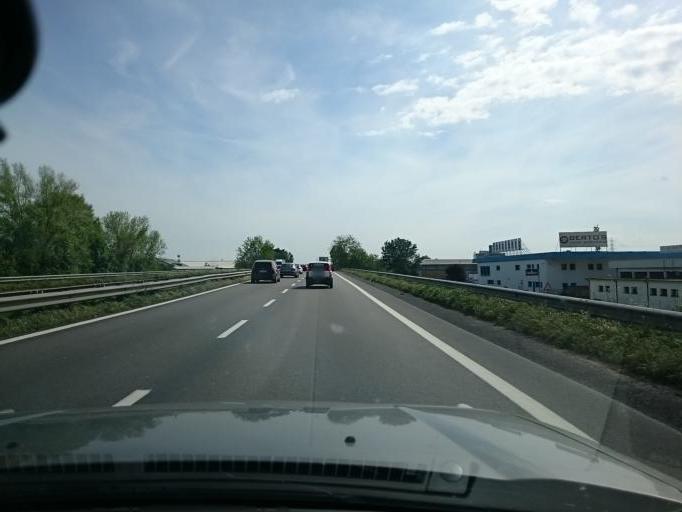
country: IT
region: Veneto
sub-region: Provincia di Padova
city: Noventa
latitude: 45.4041
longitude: 11.9319
